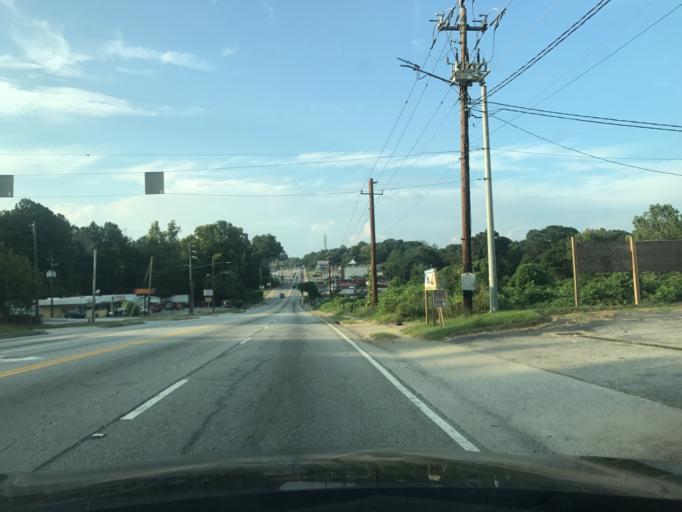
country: US
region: Georgia
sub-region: DeKalb County
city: Gresham Park
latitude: 33.7159
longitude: -84.3494
